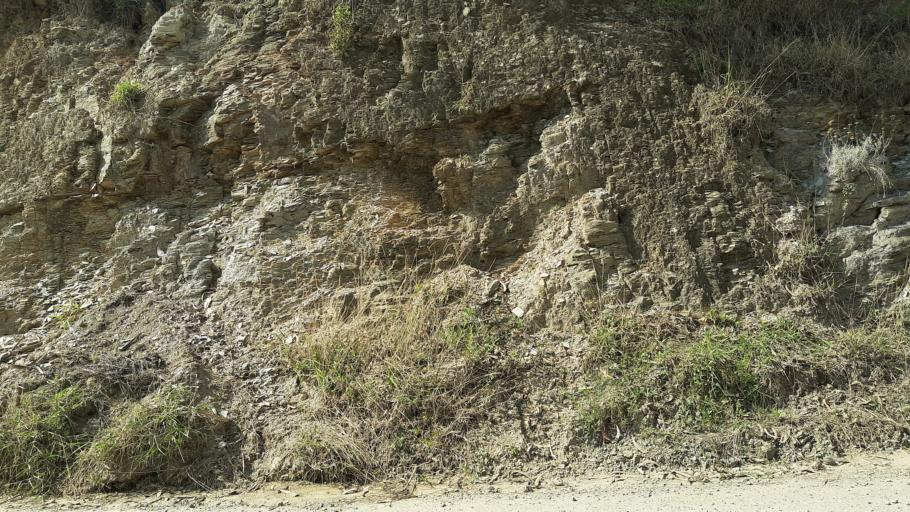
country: CO
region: Boyaca
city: Santa Sofia
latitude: 5.7642
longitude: -73.6013
